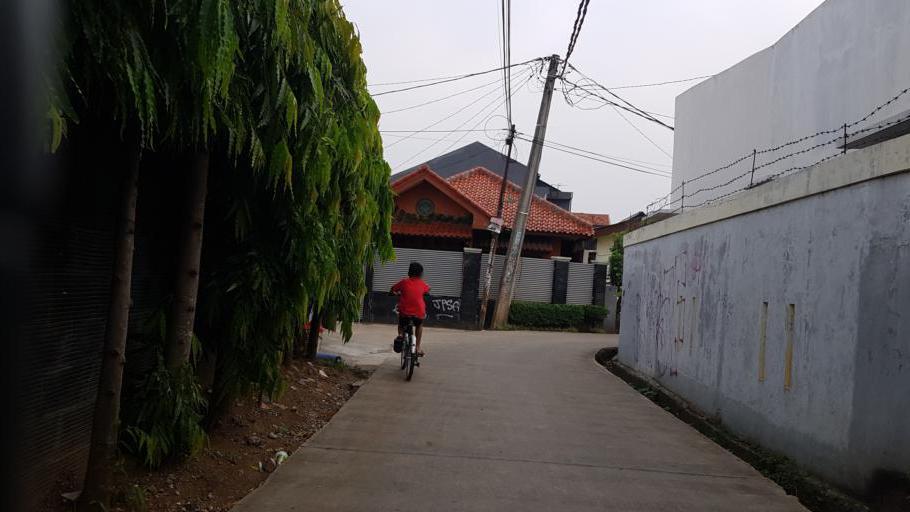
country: ID
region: West Java
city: Depok
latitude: -6.3925
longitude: 106.7995
